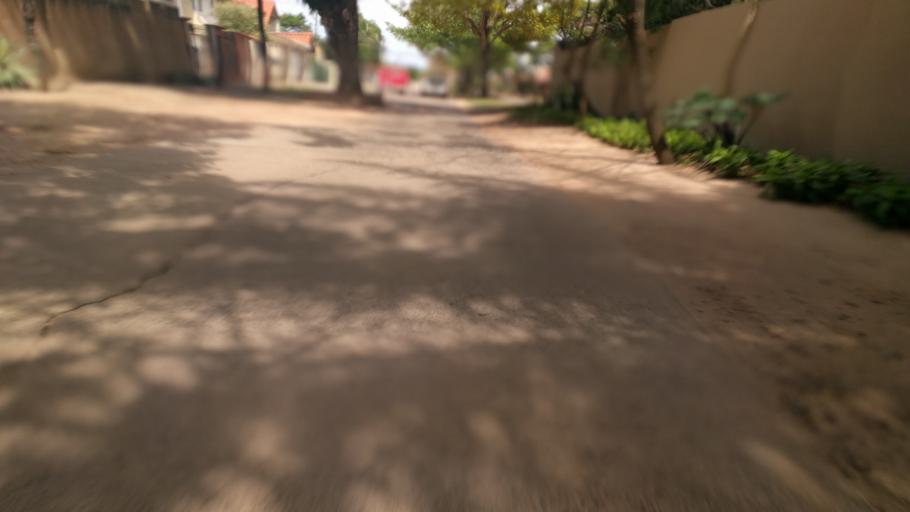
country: BO
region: Santa Cruz
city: Santa Cruz de la Sierra
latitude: -17.8181
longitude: -63.2210
